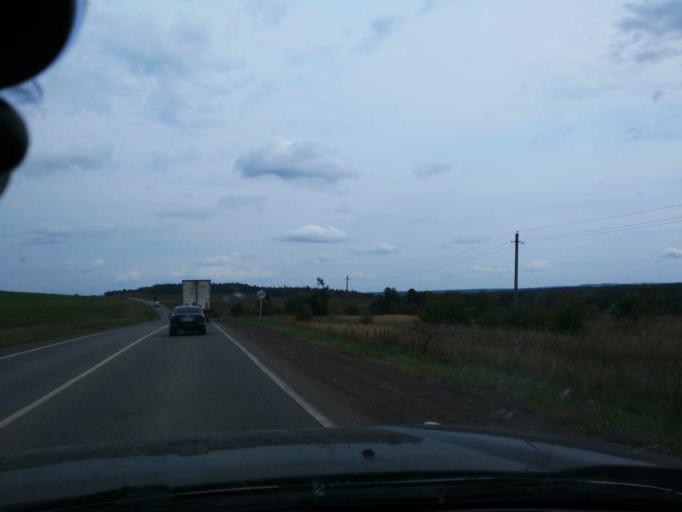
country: RU
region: Perm
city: Kuyeda
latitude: 56.4611
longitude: 55.6517
